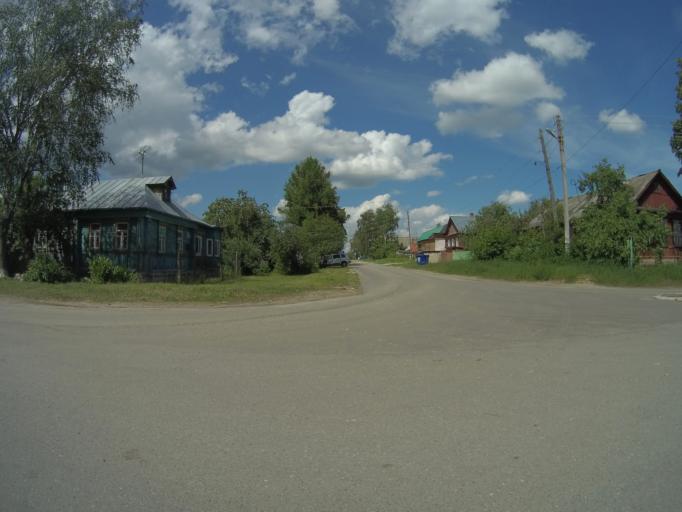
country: RU
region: Vladimir
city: Vladimir
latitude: 56.1080
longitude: 40.3636
